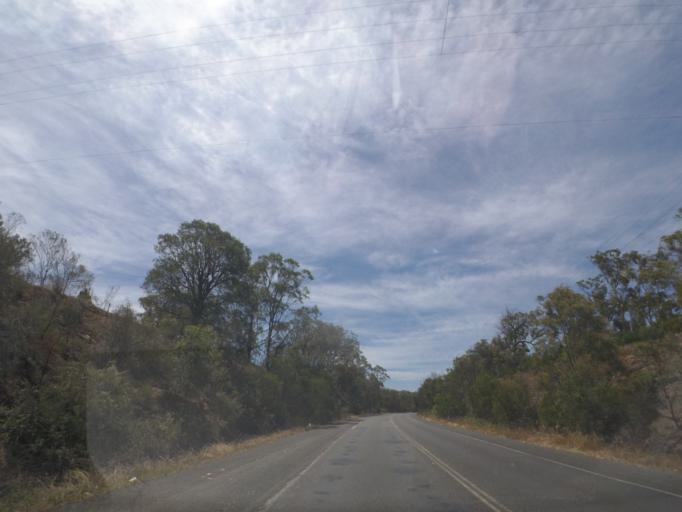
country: AU
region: New South Wales
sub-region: Wollondilly
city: Buxton
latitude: -34.2659
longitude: 150.5731
